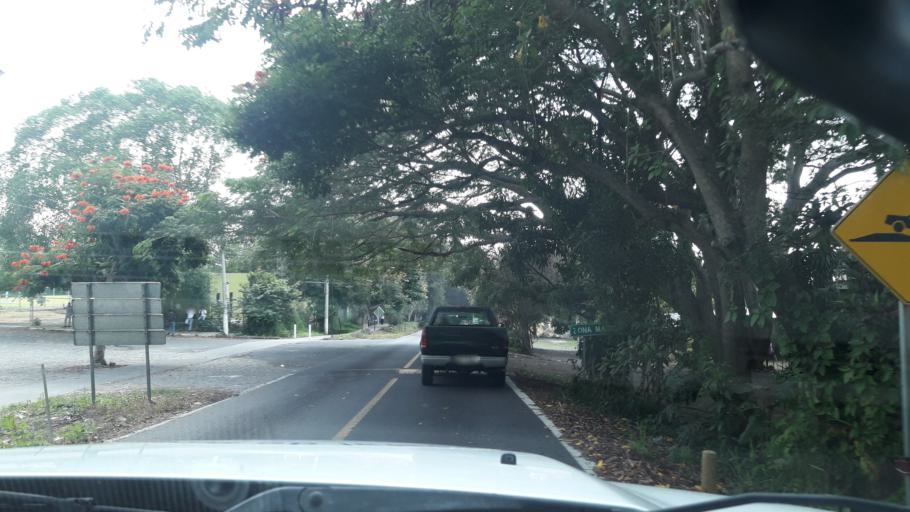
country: MX
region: Colima
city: Suchitlan
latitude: 19.3780
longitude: -103.7160
